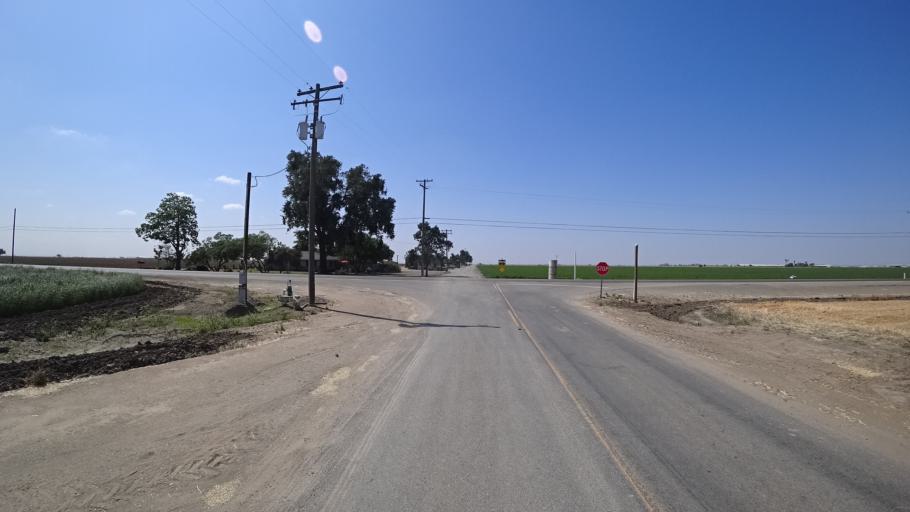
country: US
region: California
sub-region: Kings County
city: Home Garden
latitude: 36.2115
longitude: -119.6279
